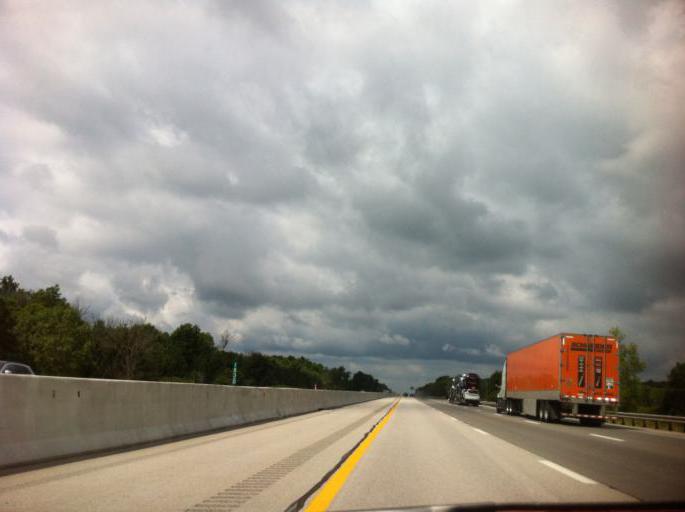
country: US
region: Ohio
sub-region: Summit County
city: Hudson
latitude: 41.2548
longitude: -81.4438
